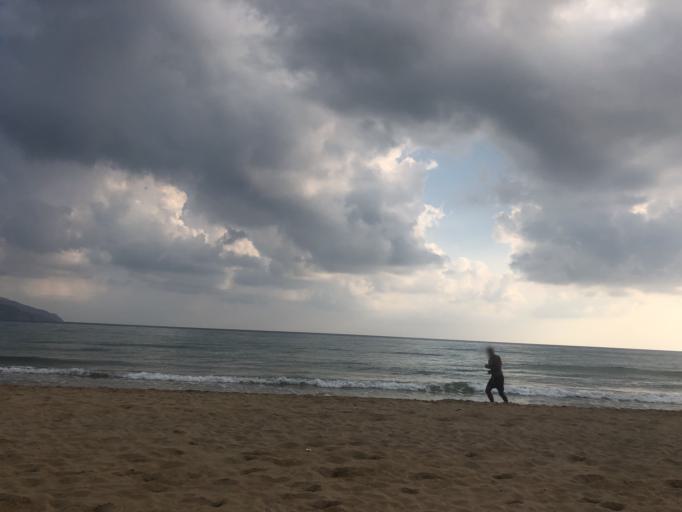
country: GR
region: Crete
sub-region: Nomos Chanias
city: Georgioupolis
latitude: 35.3567
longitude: 24.2782
